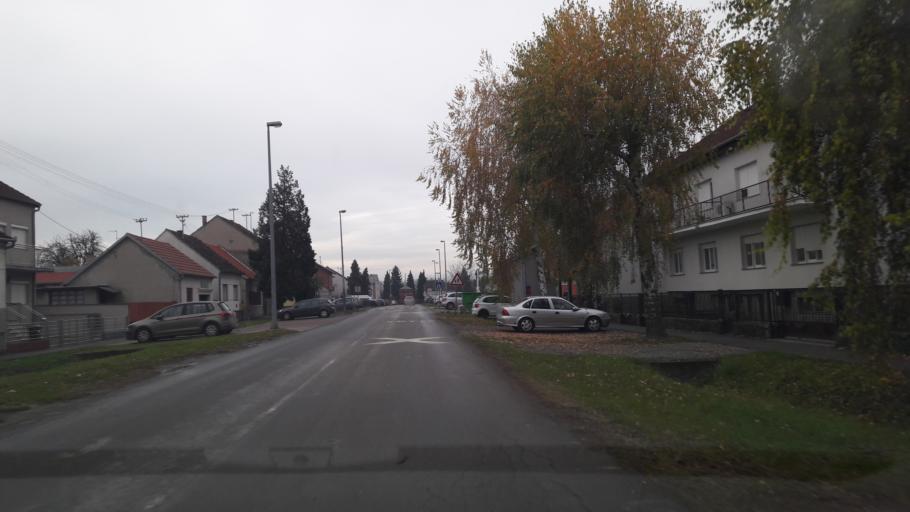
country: HR
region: Osjecko-Baranjska
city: Visnjevac
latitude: 45.5639
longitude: 18.6193
